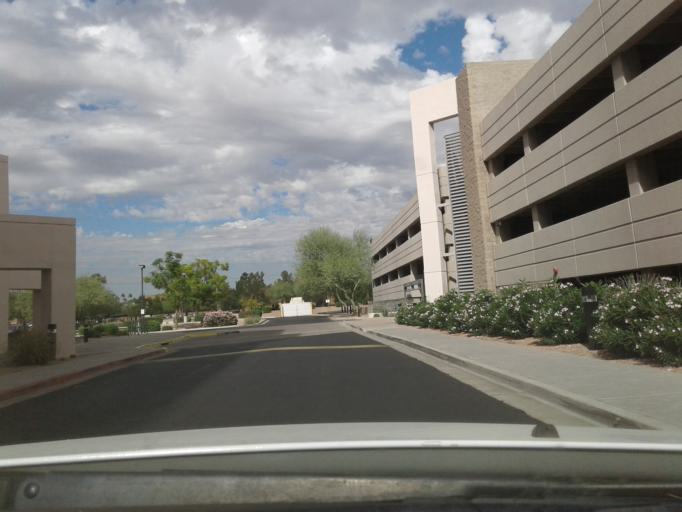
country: US
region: Arizona
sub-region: Maricopa County
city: Glendale
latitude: 33.5702
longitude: -112.1132
